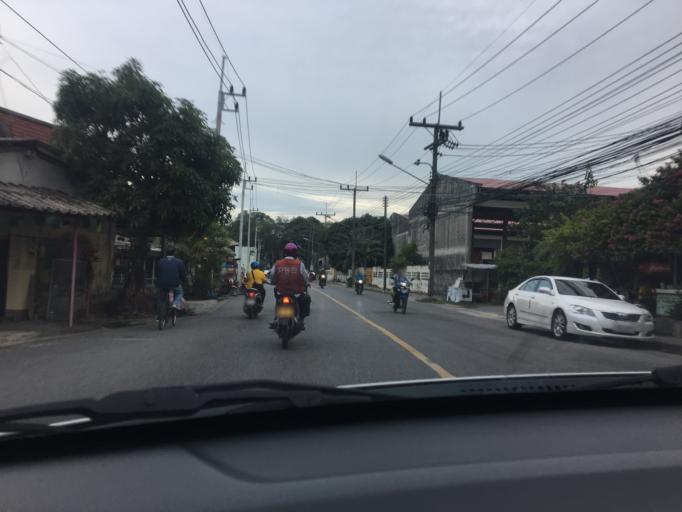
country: TH
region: Phuket
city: Phuket
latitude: 7.8969
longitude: 98.4030
